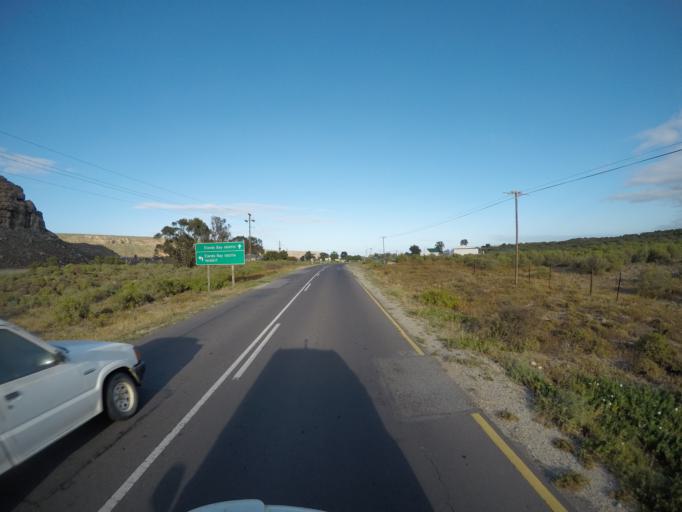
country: ZA
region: Western Cape
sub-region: West Coast District Municipality
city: Clanwilliam
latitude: -32.3131
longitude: 18.3578
